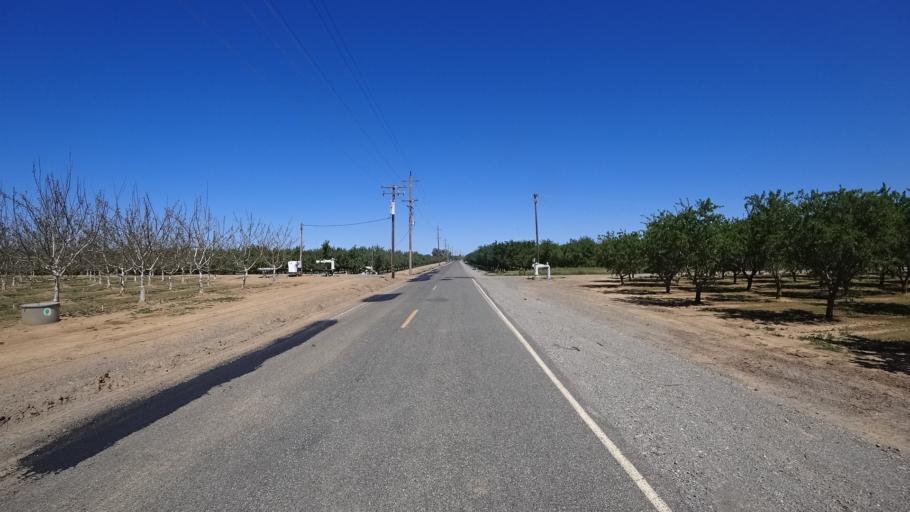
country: US
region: California
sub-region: Glenn County
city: Orland
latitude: 39.7069
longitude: -122.1783
